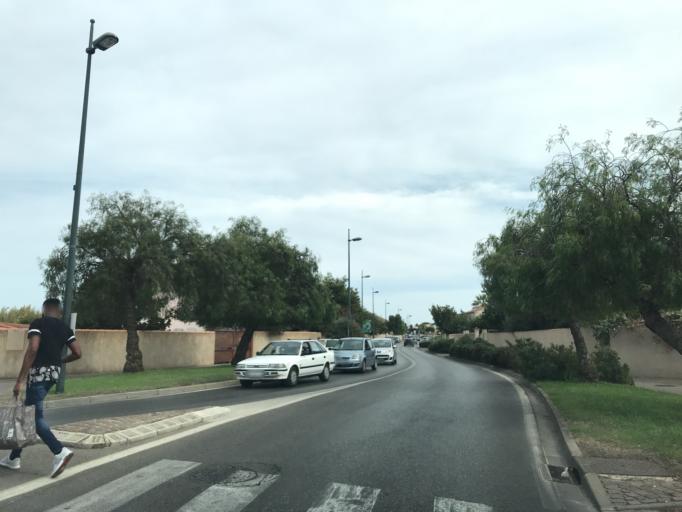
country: FR
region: Provence-Alpes-Cote d'Azur
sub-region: Departement du Var
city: Six-Fours-les-Plages
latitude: 43.0906
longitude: 5.8492
